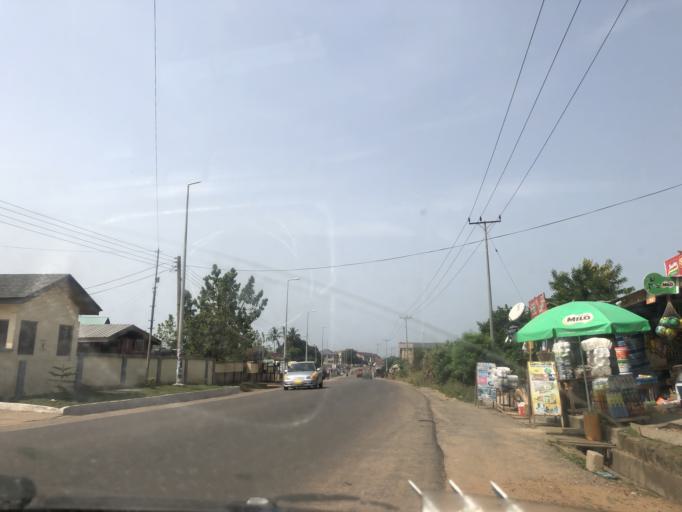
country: GH
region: Eastern
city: Koforidua
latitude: 6.0950
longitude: -0.2687
